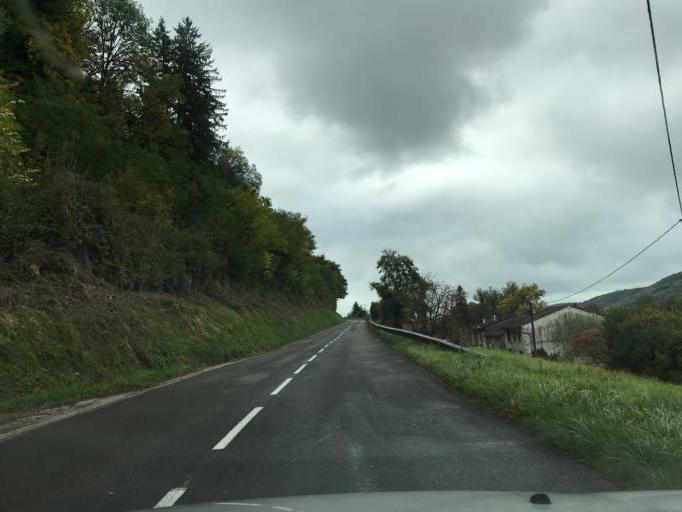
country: FR
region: Rhone-Alpes
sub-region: Departement de l'Ain
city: Coligny
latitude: 46.3980
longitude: 5.4528
